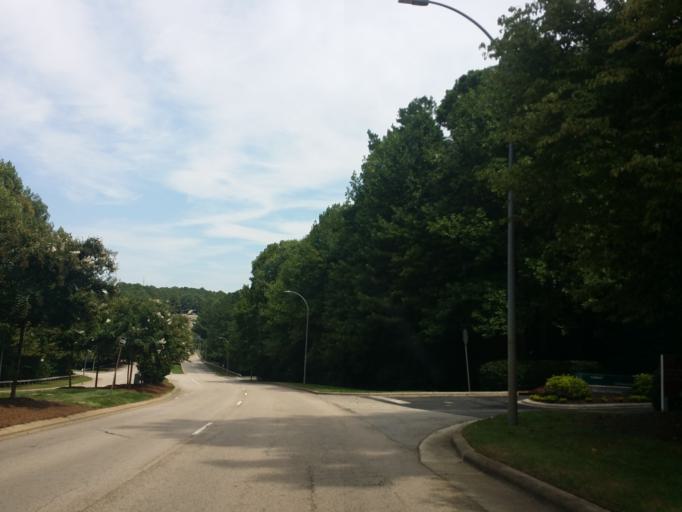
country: US
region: North Carolina
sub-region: Wake County
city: Morrisville
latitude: 35.8290
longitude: -78.7885
